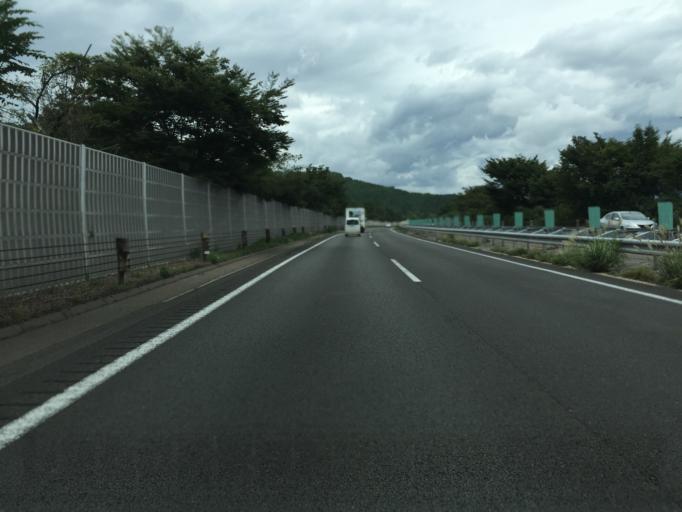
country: JP
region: Miyagi
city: Shiroishi
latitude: 37.9809
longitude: 140.6089
